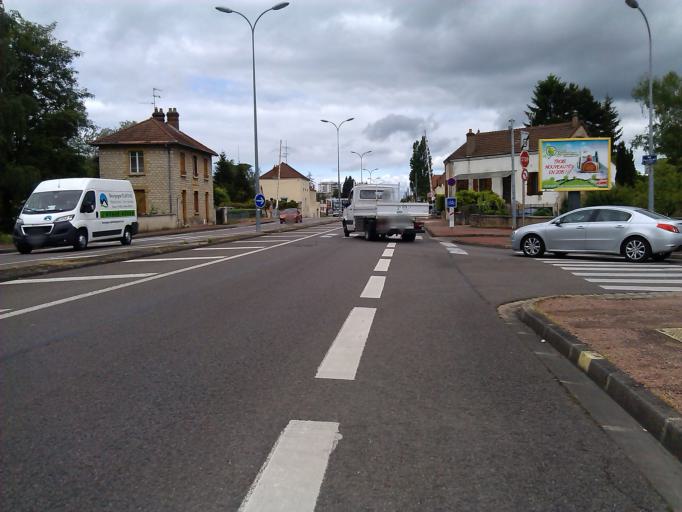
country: FR
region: Bourgogne
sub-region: Departement de Saone-et-Loire
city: Chalon-sur-Saone
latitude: 46.7996
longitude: 4.8466
